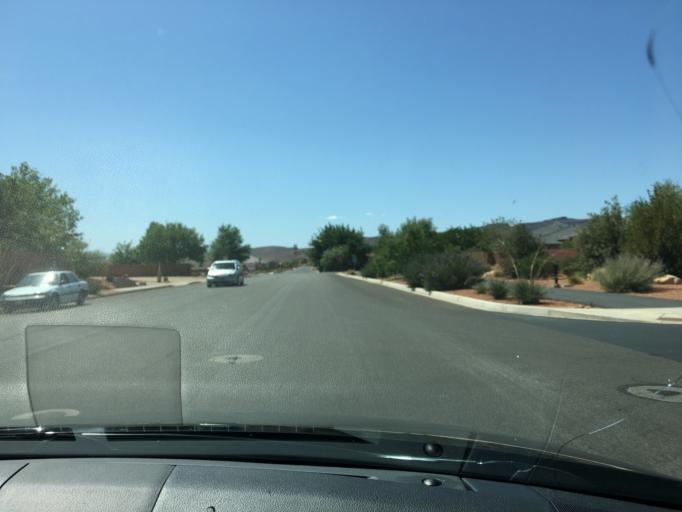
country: US
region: Utah
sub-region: Washington County
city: Ivins
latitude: 37.1620
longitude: -113.6887
